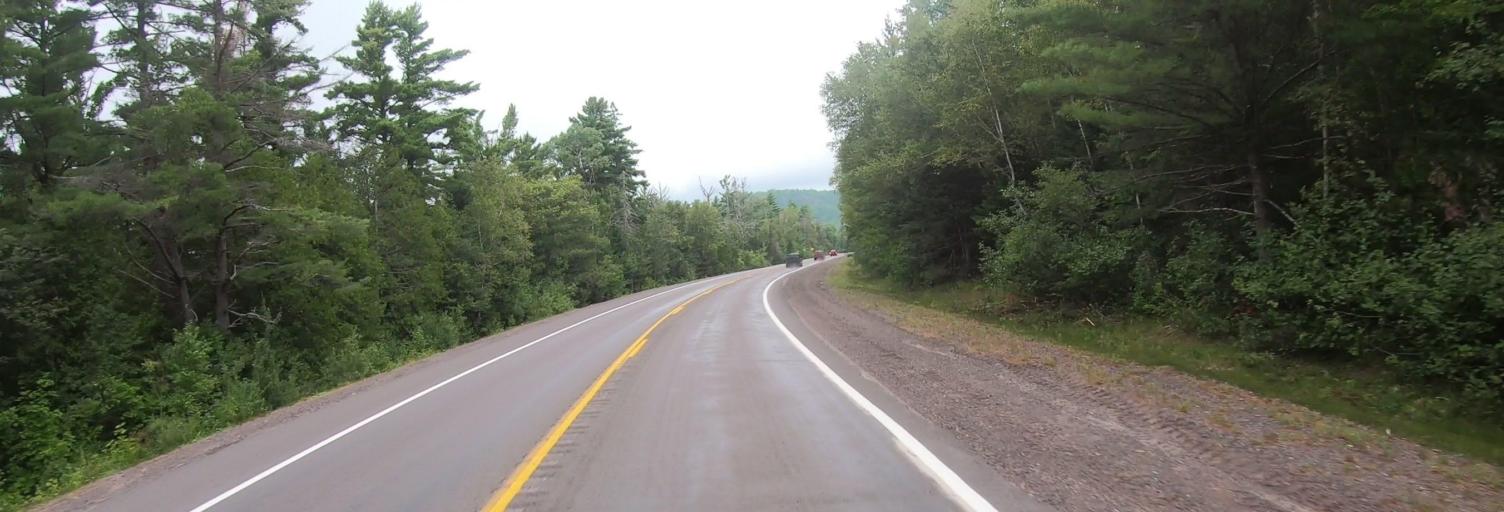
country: US
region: Michigan
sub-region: Keweenaw County
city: Eagle River
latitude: 47.3676
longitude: -88.3070
